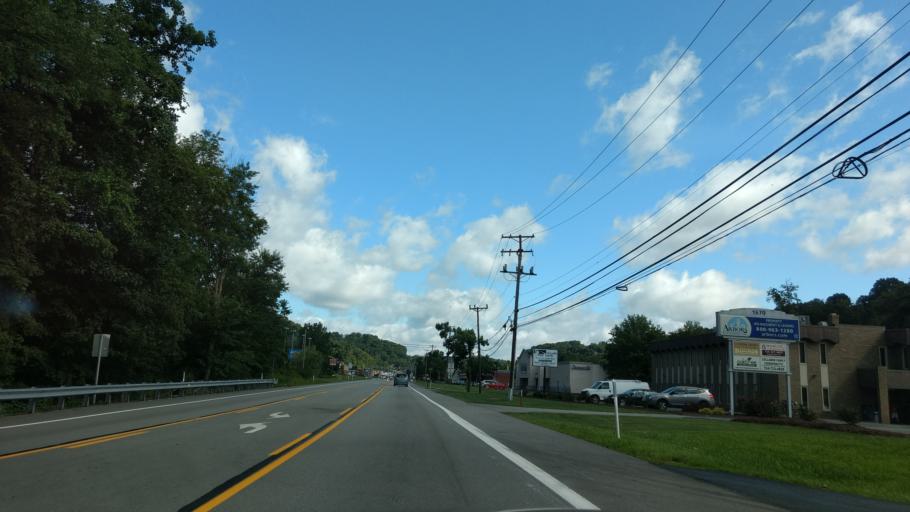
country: US
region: Pennsylvania
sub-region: Westmoreland County
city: Murrysville
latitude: 40.4387
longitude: -79.7128
